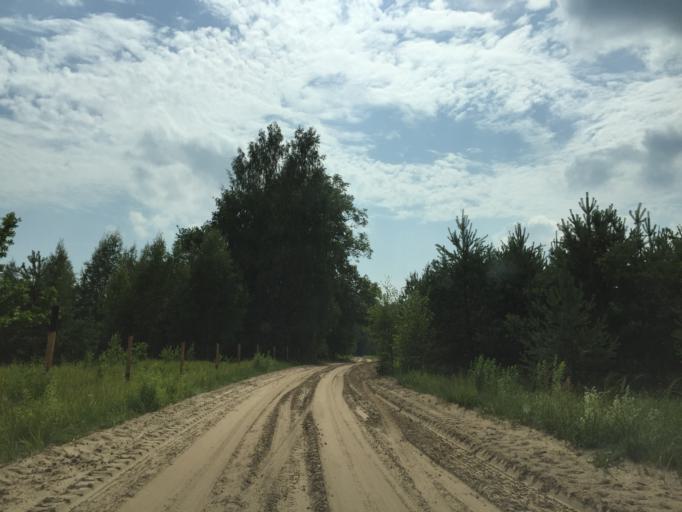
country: LV
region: Ozolnieku
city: Ozolnieki
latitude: 56.7582
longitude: 23.7531
